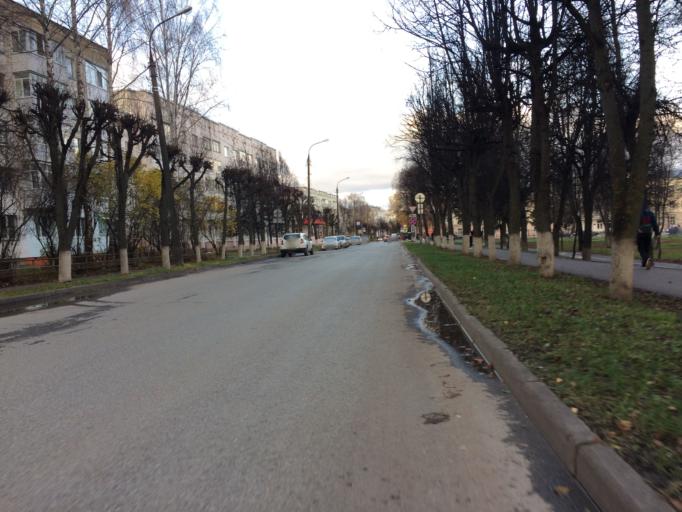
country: RU
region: Mariy-El
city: Yoshkar-Ola
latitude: 56.6271
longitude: 47.8899
